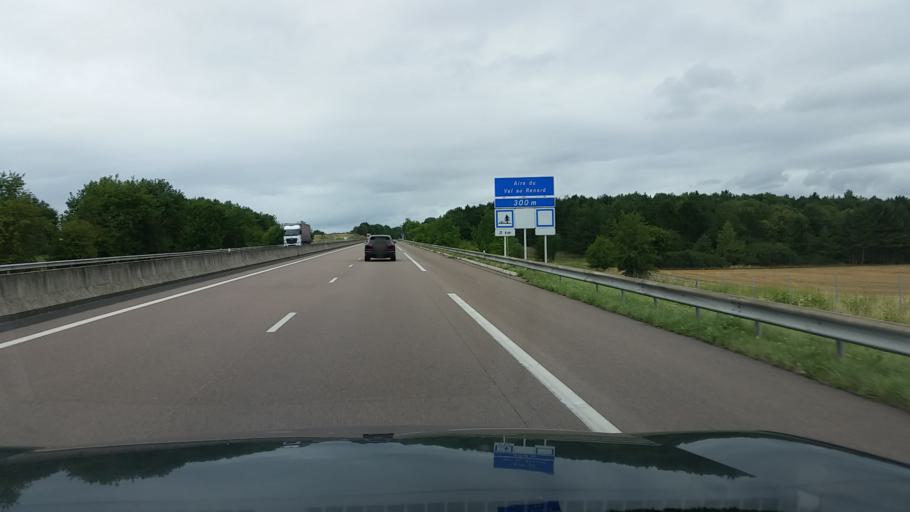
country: FR
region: Lorraine
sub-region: Departement de Meurthe-et-Moselle
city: Colombey-les-Belles
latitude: 48.4180
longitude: 5.8632
